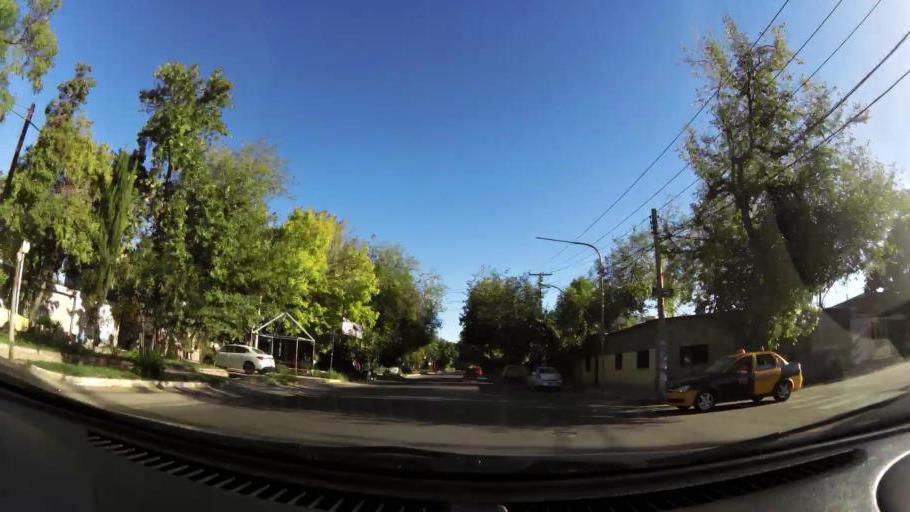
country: AR
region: Mendoza
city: Las Heras
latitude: -32.8644
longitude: -68.8286
